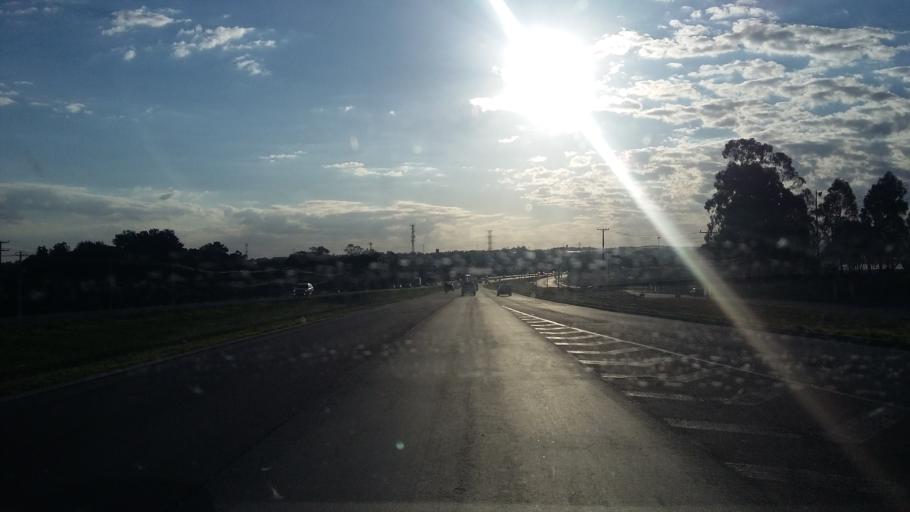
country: BR
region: Parana
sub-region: Araucaria
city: Araucaria
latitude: -25.5327
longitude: -49.3207
